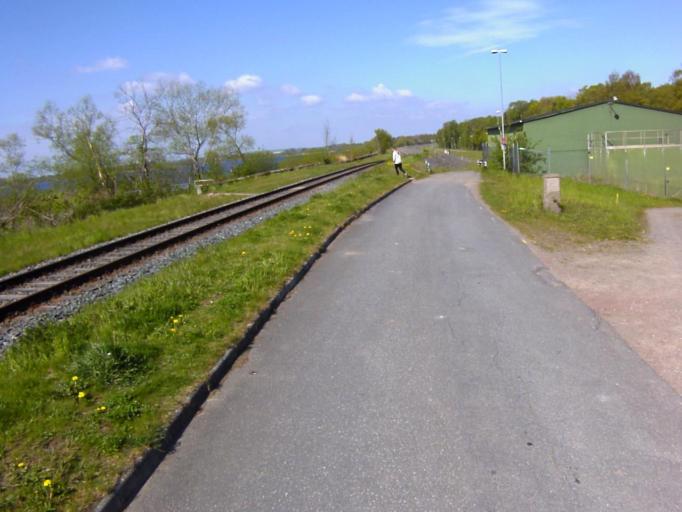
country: SE
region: Skane
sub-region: Kristianstads Kommun
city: Kristianstad
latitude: 56.0142
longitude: 14.1873
